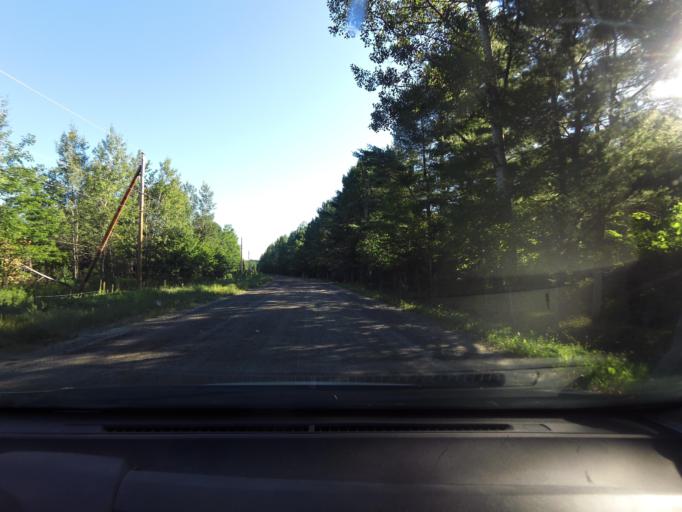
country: CA
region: Quebec
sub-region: Mauricie
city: Becancour
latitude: 46.5459
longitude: -72.3962
